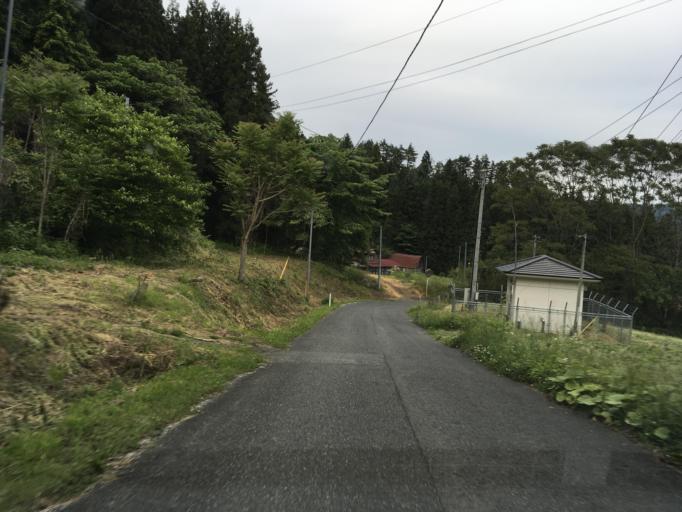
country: JP
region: Iwate
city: Mizusawa
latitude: 39.1598
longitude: 141.2998
